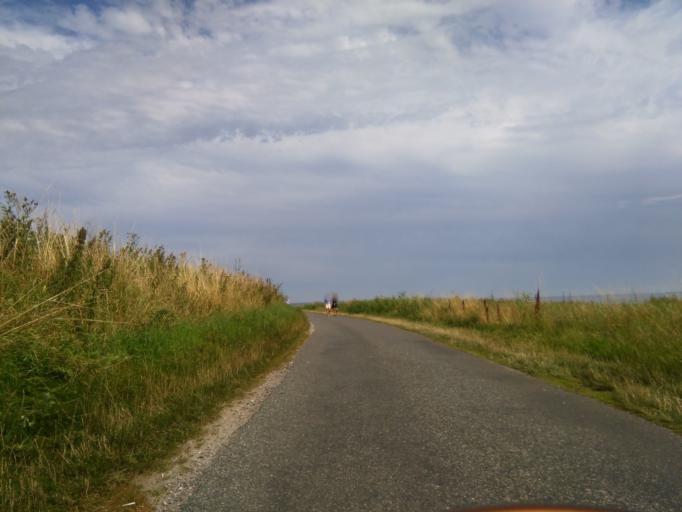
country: DK
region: Central Jutland
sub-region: Hedensted Kommune
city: Juelsminde
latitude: 55.8432
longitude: 10.0431
